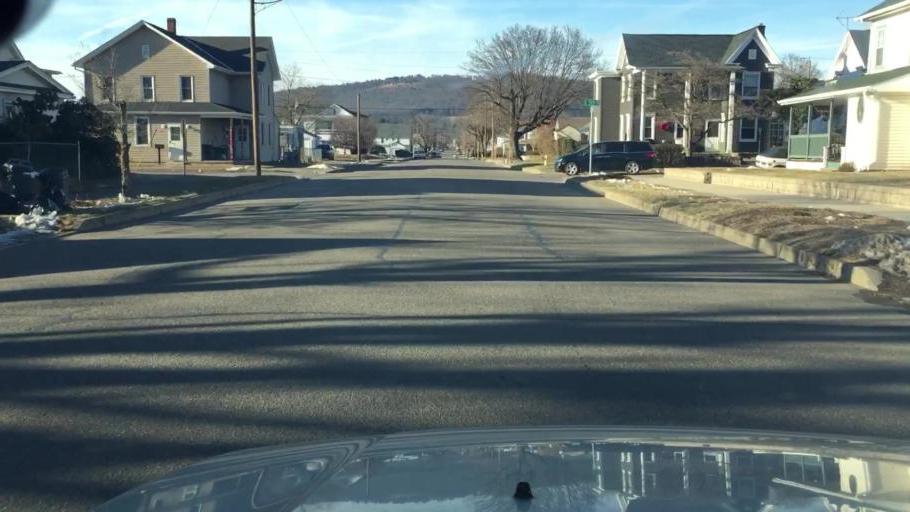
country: US
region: Pennsylvania
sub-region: Columbia County
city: Berwick
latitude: 41.0596
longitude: -76.2304
